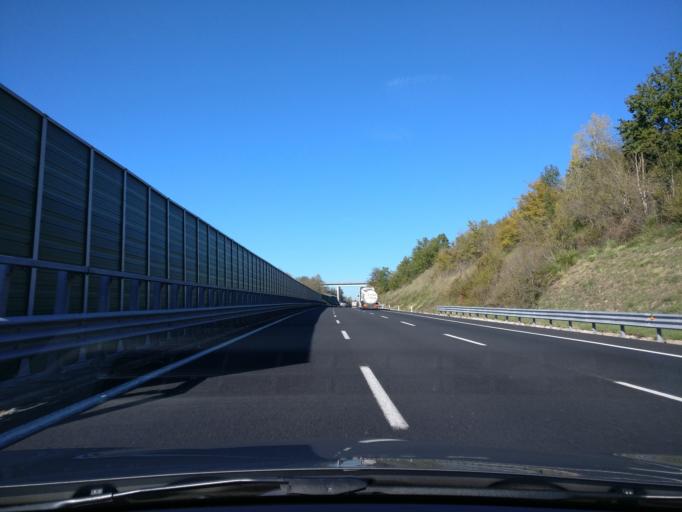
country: IT
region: Latium
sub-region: Provincia di Frosinone
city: Arnara
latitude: 41.5787
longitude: 13.3632
